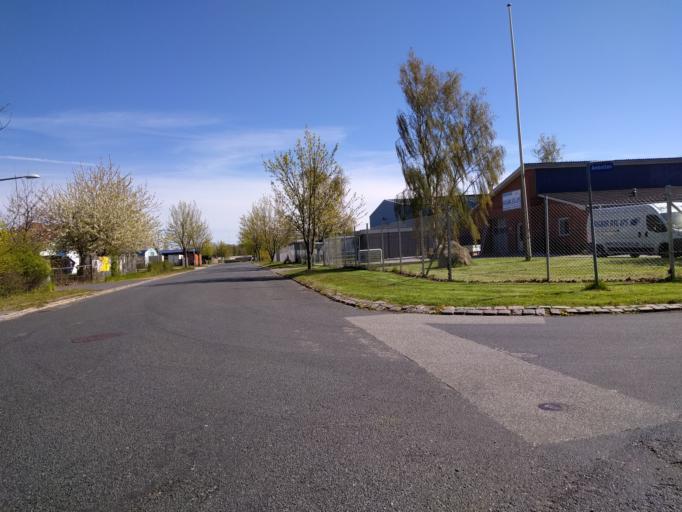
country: DK
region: South Denmark
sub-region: Kerteminde Kommune
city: Munkebo
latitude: 55.4625
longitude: 10.5451
